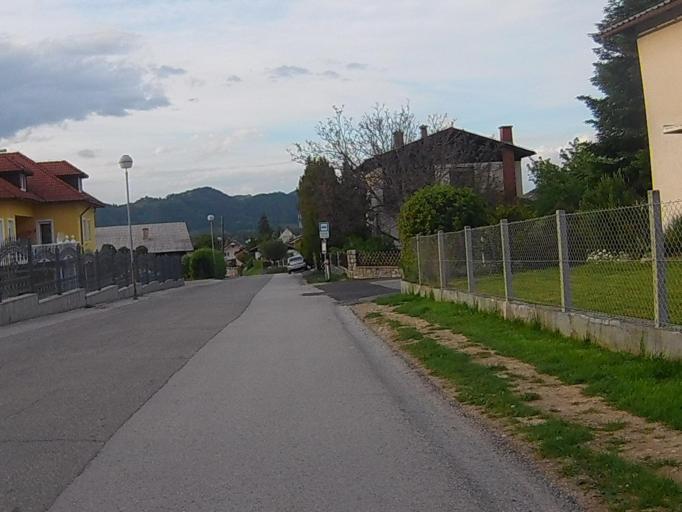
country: SI
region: Maribor
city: Pekre
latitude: 46.5464
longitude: 15.5892
